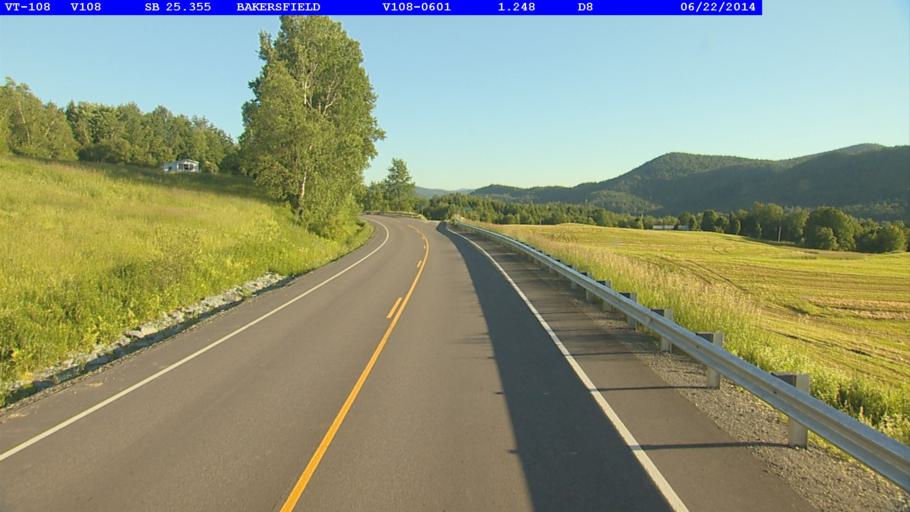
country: US
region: Vermont
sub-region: Franklin County
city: Enosburg Falls
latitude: 44.7512
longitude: -72.8234
